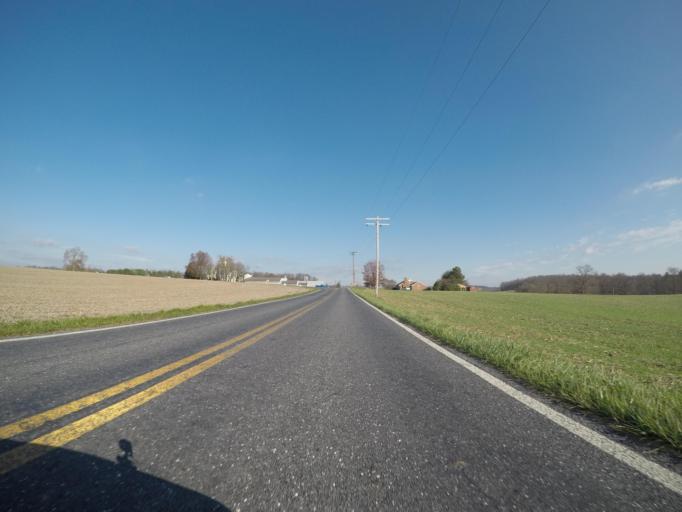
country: US
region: Maryland
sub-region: Carroll County
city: Hampstead
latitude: 39.5539
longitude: -76.8795
